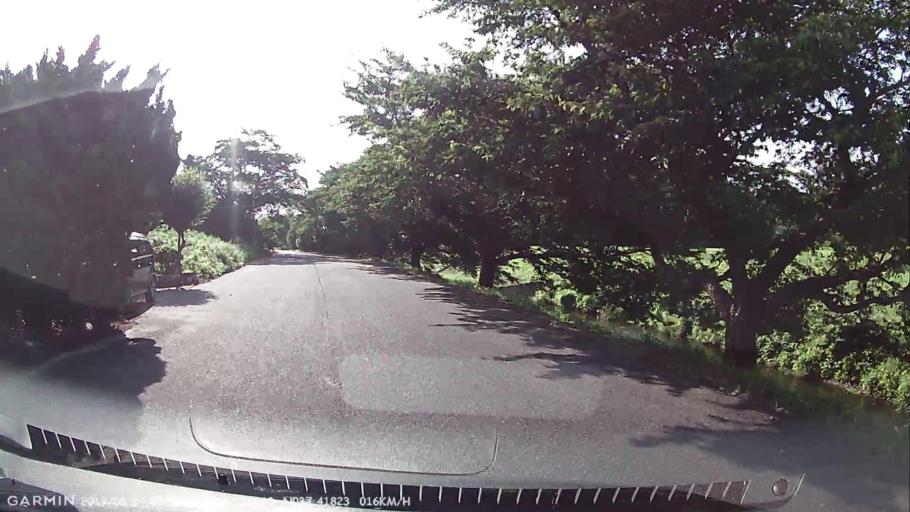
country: JP
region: Fukushima
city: Koriyama
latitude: 37.4182
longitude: 140.2666
